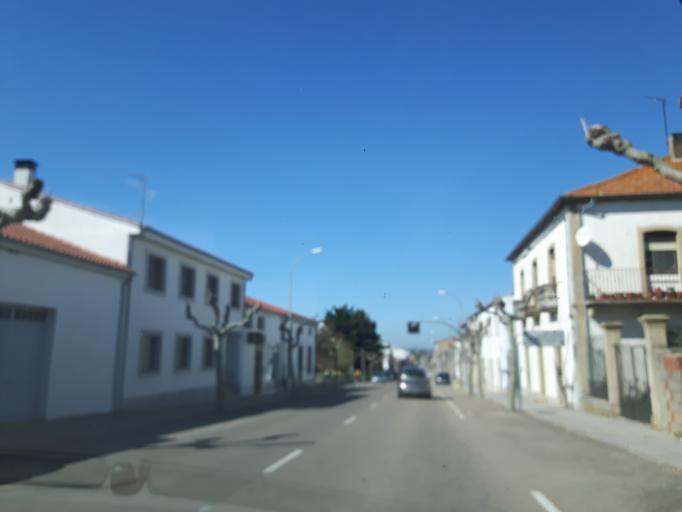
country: ES
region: Castille and Leon
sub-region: Provincia de Salamanca
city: Lumbrales
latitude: 40.9362
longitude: -6.7153
